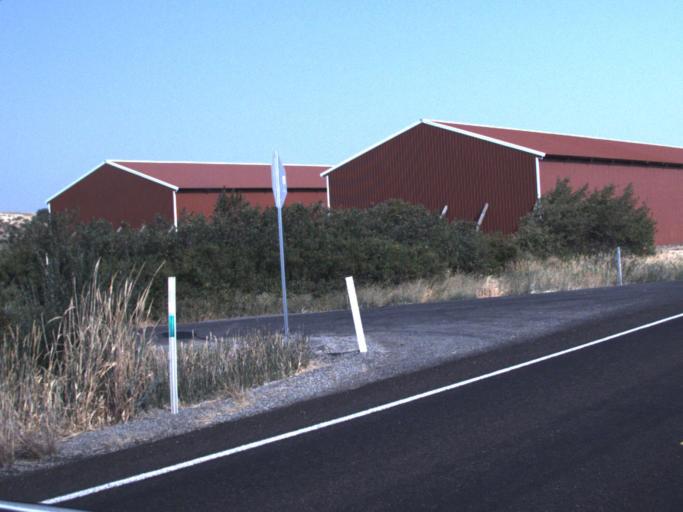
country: US
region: Washington
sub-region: Kittitas County
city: Ellensburg
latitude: 47.0441
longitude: -120.6247
